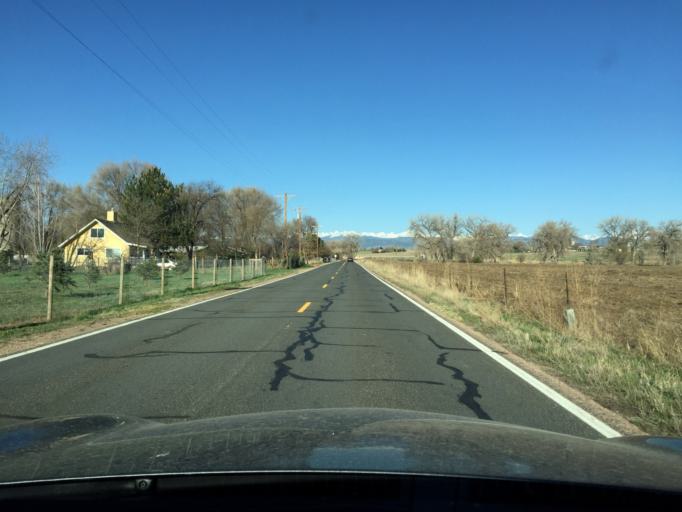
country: US
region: Colorado
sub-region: Boulder County
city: Erie
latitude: 40.0695
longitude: -105.0782
